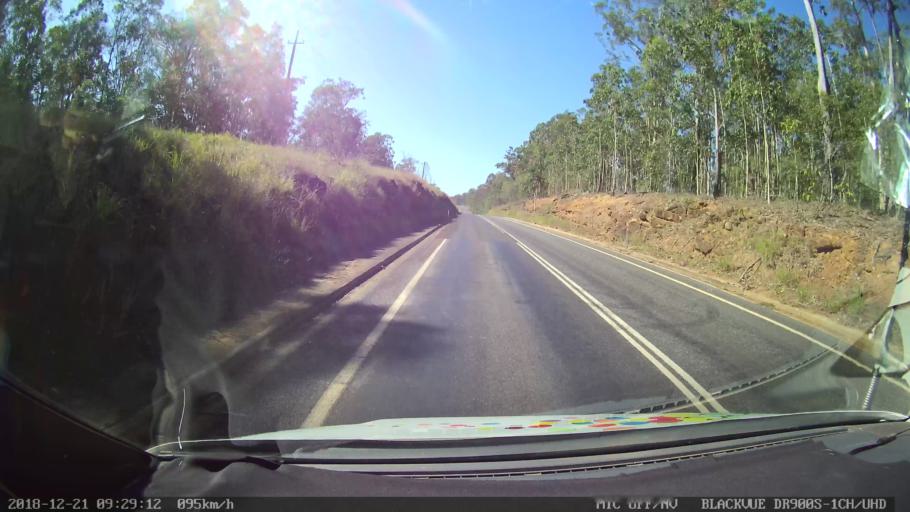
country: AU
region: New South Wales
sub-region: Clarence Valley
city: Maclean
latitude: -29.4284
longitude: 152.9888
